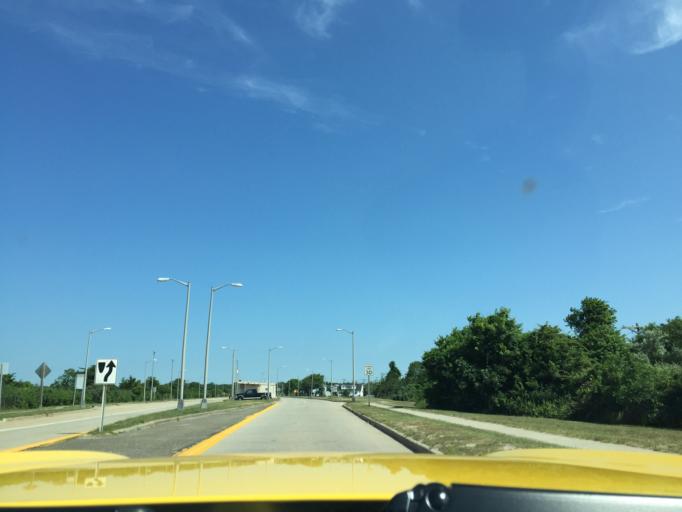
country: US
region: New York
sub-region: Suffolk County
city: Mastic Beach
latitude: 40.7405
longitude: -72.8692
